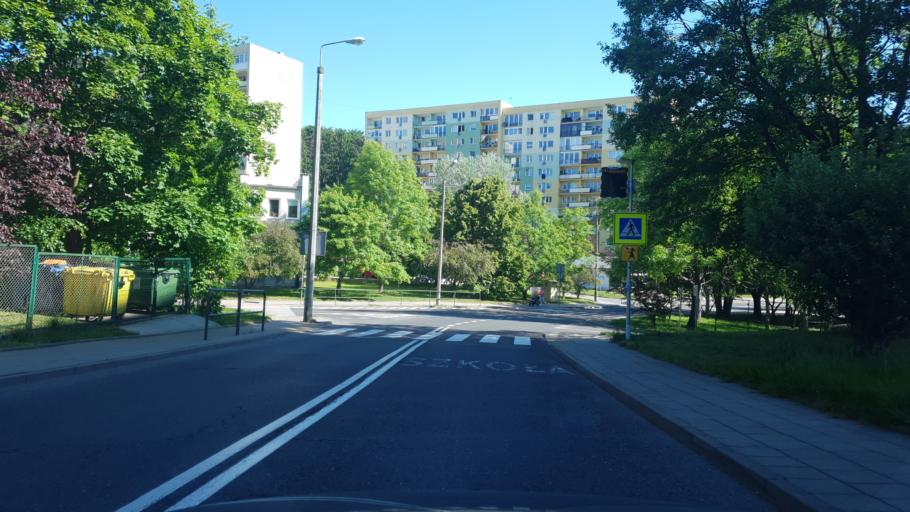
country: PL
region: Pomeranian Voivodeship
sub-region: Sopot
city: Sopot
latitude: 54.4568
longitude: 18.5334
